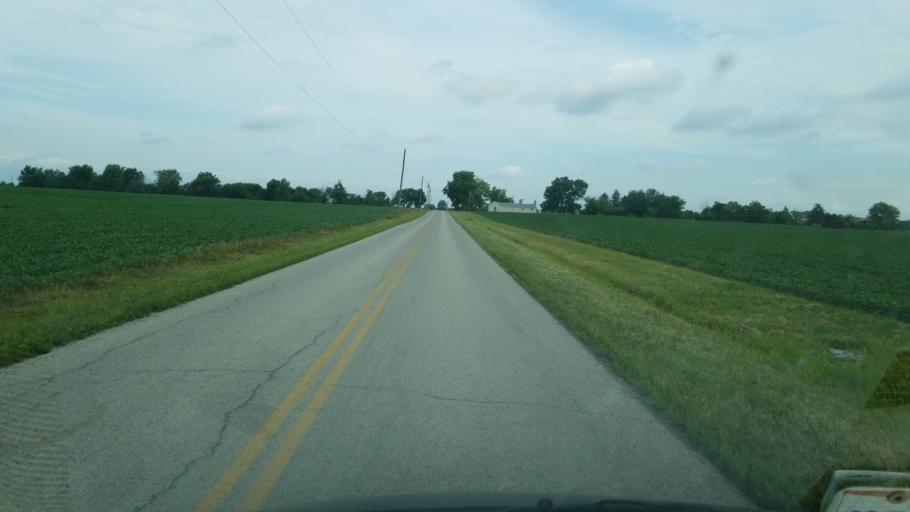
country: US
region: Ohio
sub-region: Seneca County
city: Tiffin
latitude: 41.0911
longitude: -83.0930
